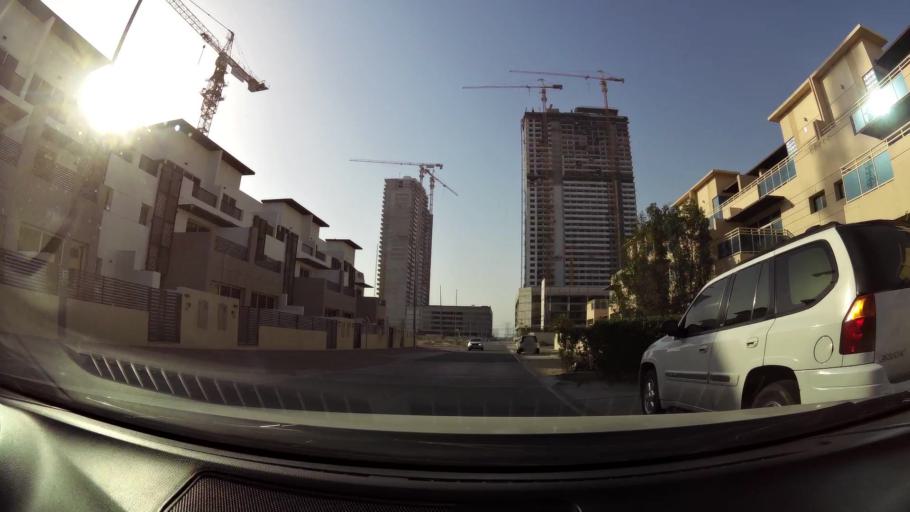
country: AE
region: Dubai
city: Dubai
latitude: 25.0507
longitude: 55.1995
